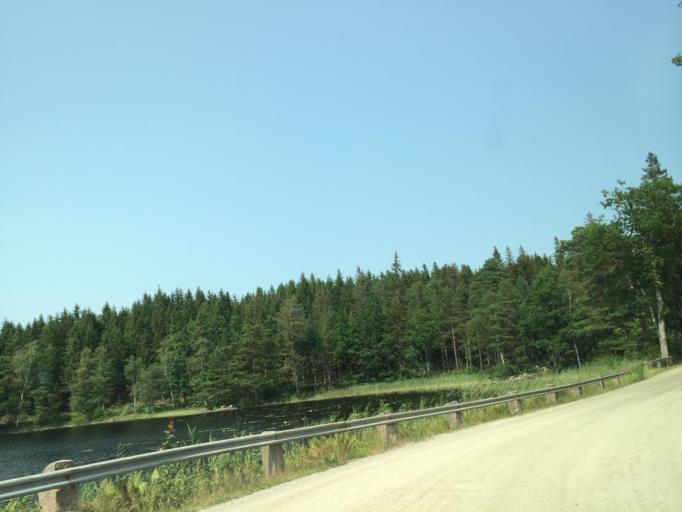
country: SE
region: Vaestra Goetaland
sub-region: Lilla Edets Kommun
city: Lilla Edet
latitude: 58.2302
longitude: 12.1156
